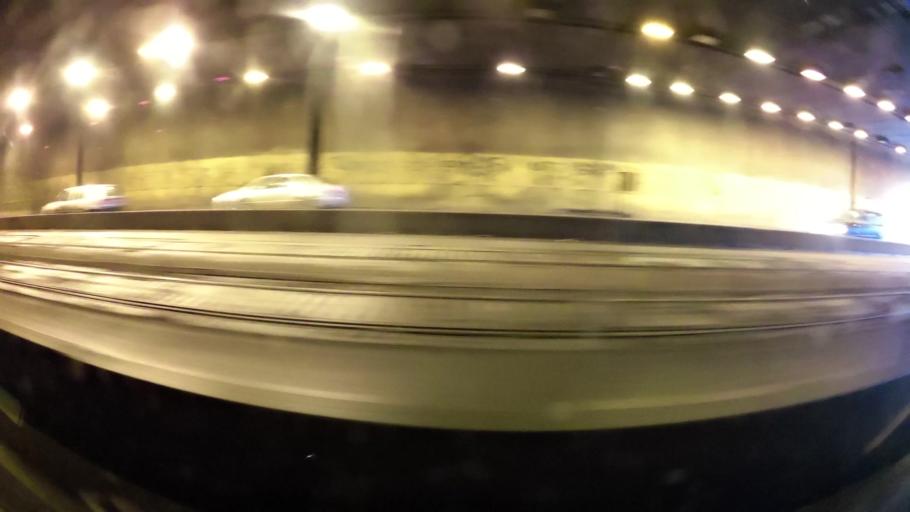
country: BG
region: Sofia-Capital
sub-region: Stolichna Obshtina
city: Sofia
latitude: 42.7091
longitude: 23.2747
